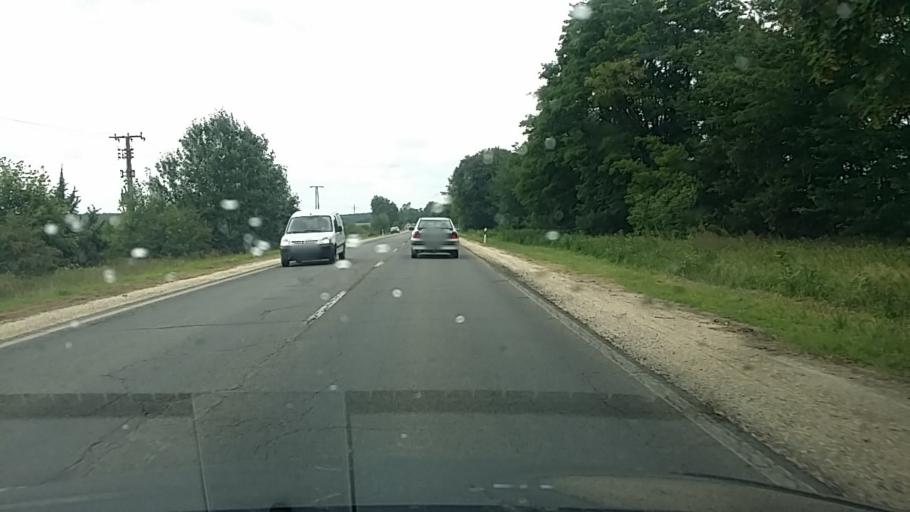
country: HU
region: Pest
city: Orkeny
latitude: 47.1362
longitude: 19.4106
